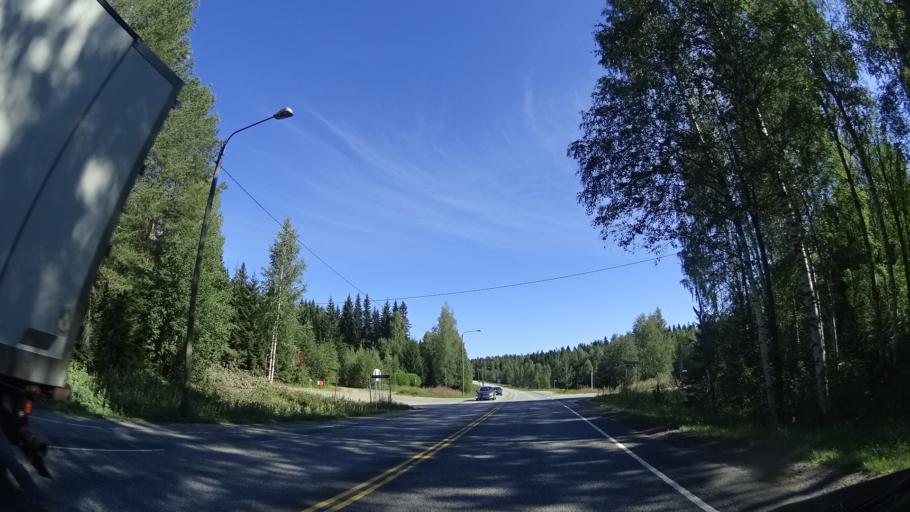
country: FI
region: Central Finland
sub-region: AEaenekoski
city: AEaenekoski
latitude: 62.8275
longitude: 25.8129
